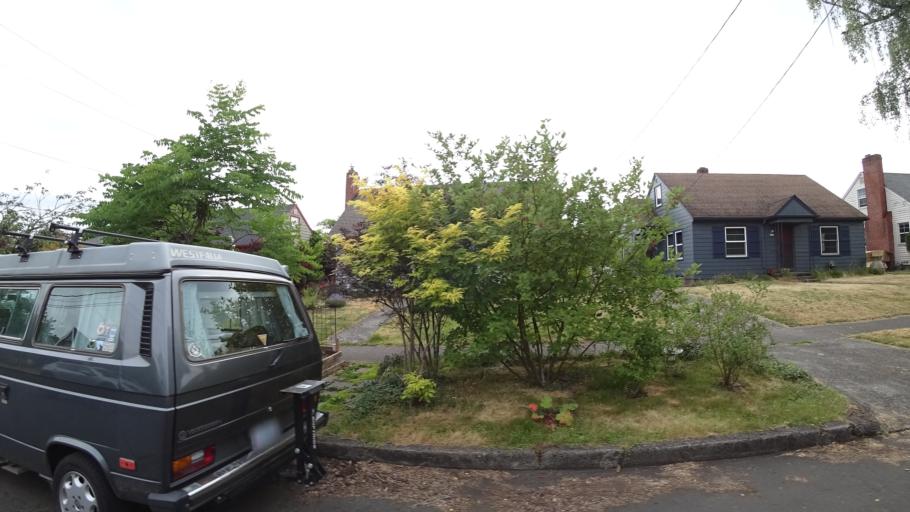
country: US
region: Oregon
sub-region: Multnomah County
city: Portland
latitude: 45.5742
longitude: -122.6833
